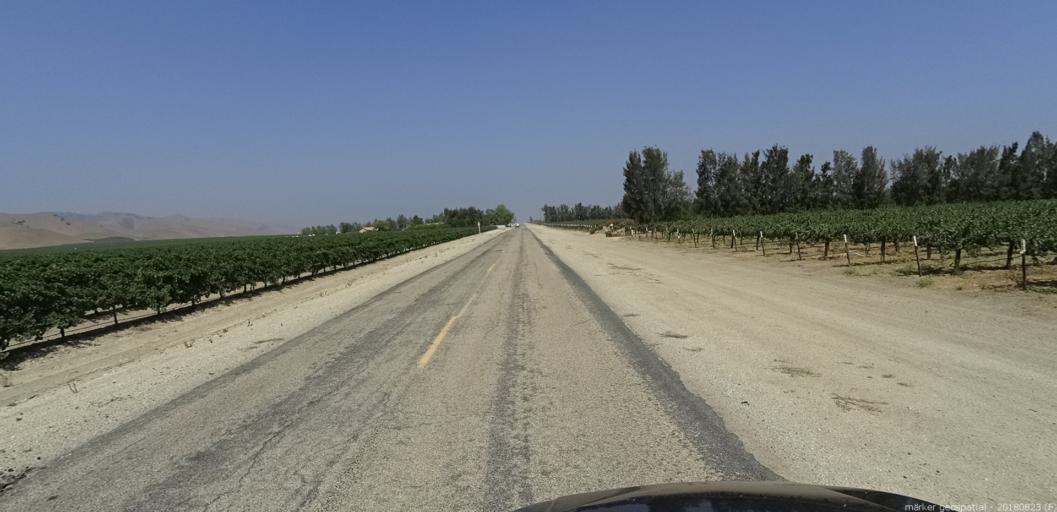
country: US
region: California
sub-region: Monterey County
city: King City
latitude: 36.2474
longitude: -121.1929
